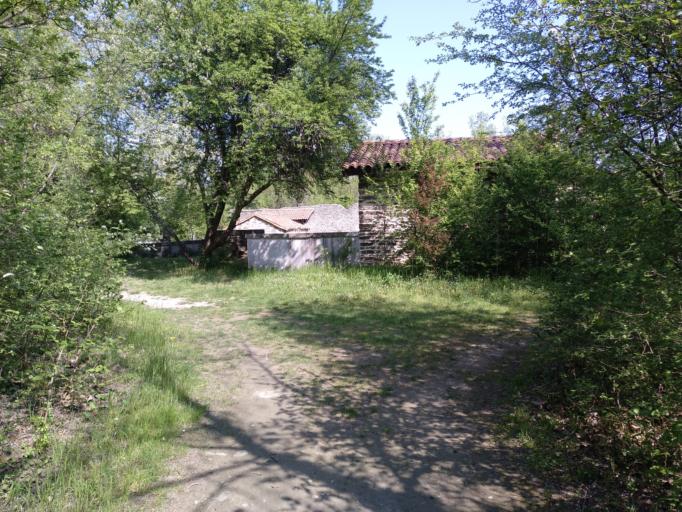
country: FR
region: Rhone-Alpes
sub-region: Departement du Rhone
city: Serezin-du-Rhone
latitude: 45.6301
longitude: 4.8097
